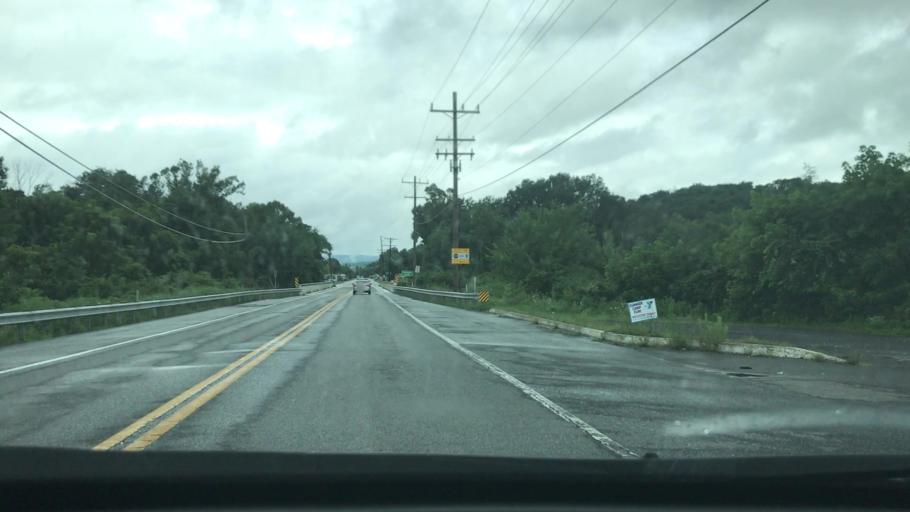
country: US
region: Maryland
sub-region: Washington County
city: Hancock
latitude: 39.6954
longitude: -78.1553
